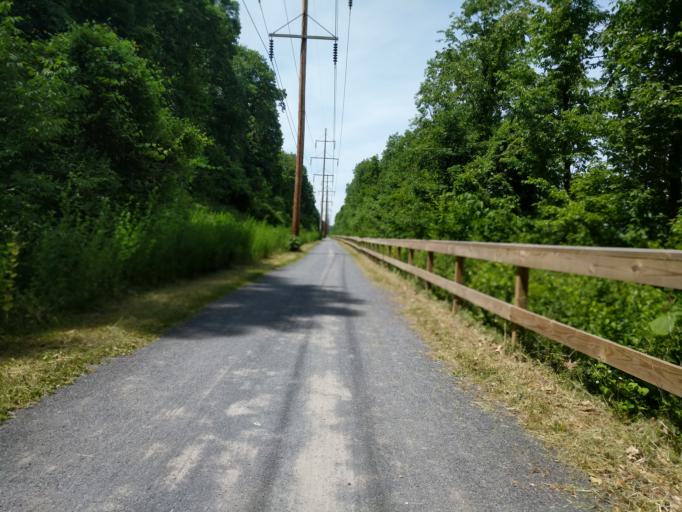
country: US
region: New York
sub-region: Tompkins County
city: Northwest Ithaca
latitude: 42.4602
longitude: -76.5221
